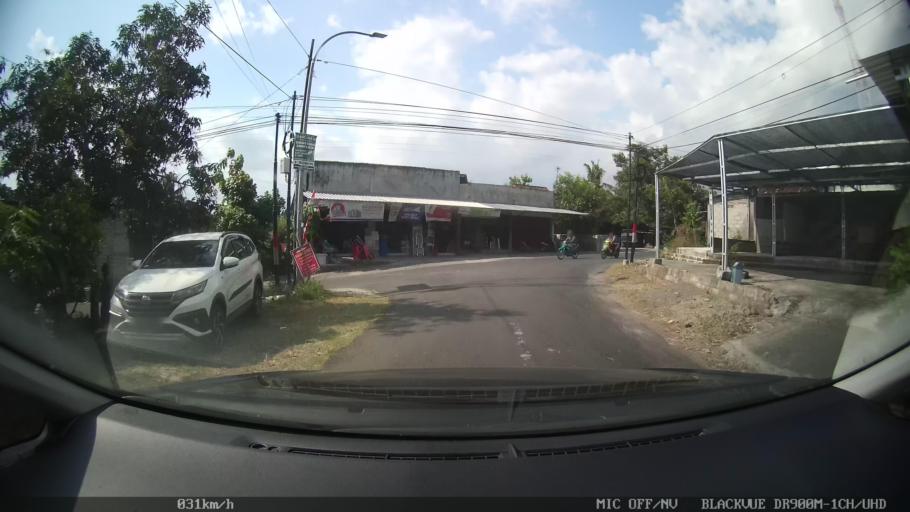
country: ID
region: Daerah Istimewa Yogyakarta
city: Kasihan
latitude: -7.8426
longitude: 110.3040
